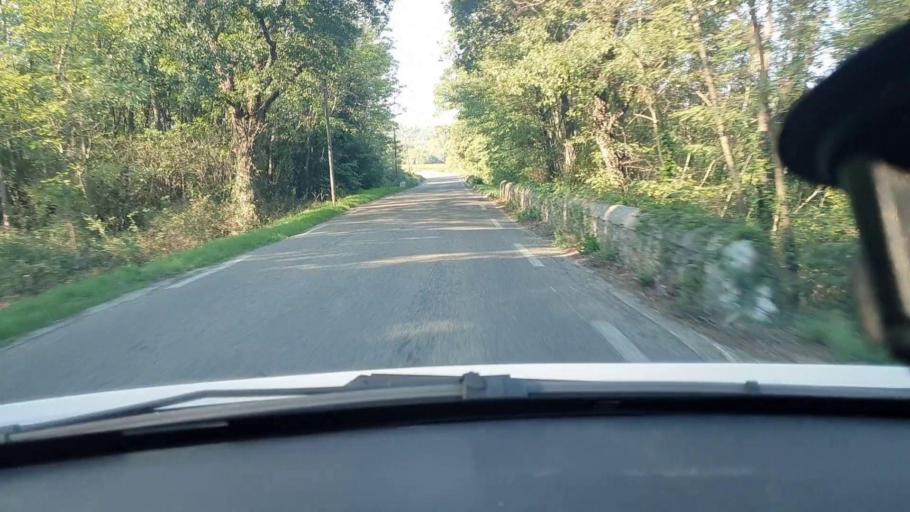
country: FR
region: Languedoc-Roussillon
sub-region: Departement du Gard
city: Goudargues
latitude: 44.1881
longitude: 4.4806
